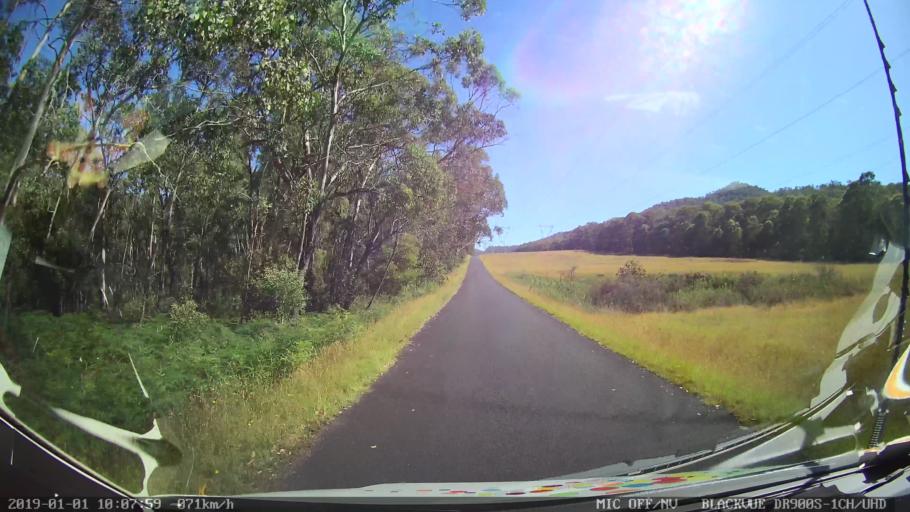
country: AU
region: New South Wales
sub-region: Snowy River
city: Jindabyne
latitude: -36.1639
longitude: 148.1573
